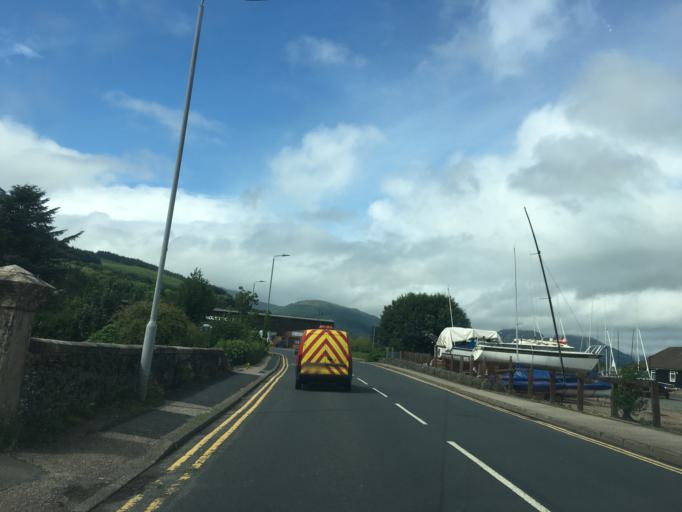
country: GB
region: Scotland
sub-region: Argyll and Bute
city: Dunoon
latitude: 55.9812
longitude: -4.9456
